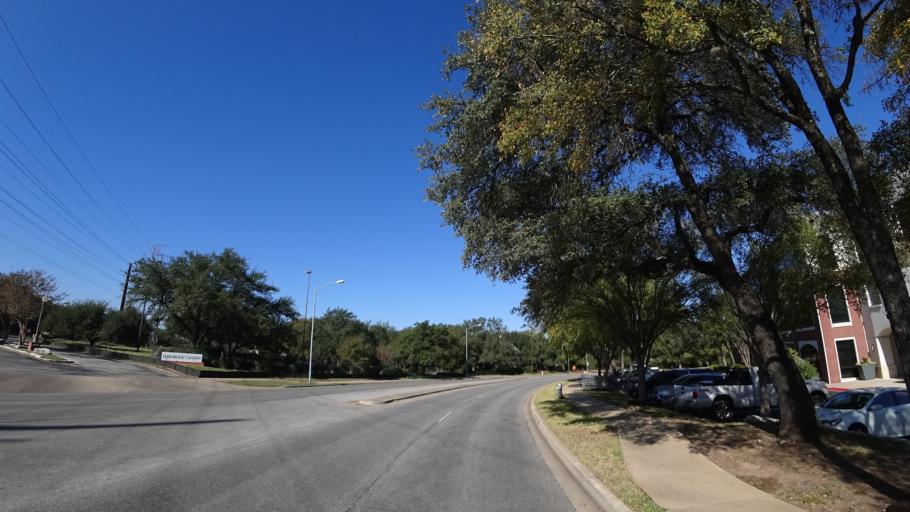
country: US
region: Texas
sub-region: Williamson County
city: Jollyville
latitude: 30.4009
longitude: -97.7515
